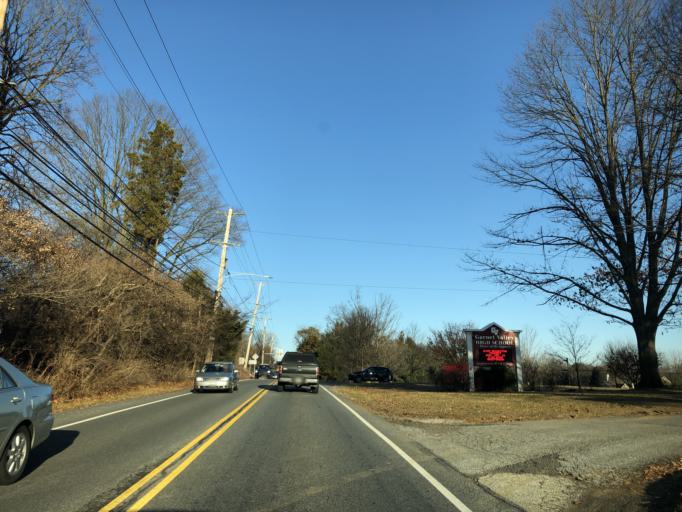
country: US
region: Pennsylvania
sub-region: Delaware County
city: Chester Heights
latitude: 39.8695
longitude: -75.5069
